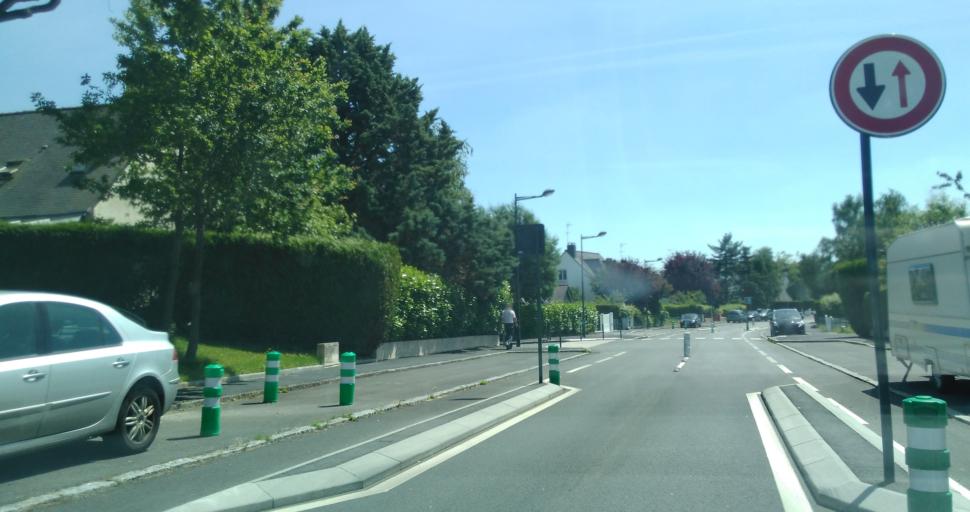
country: FR
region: Brittany
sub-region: Departement d'Ille-et-Vilaine
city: Chantepie
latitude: 48.0911
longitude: -1.6078
